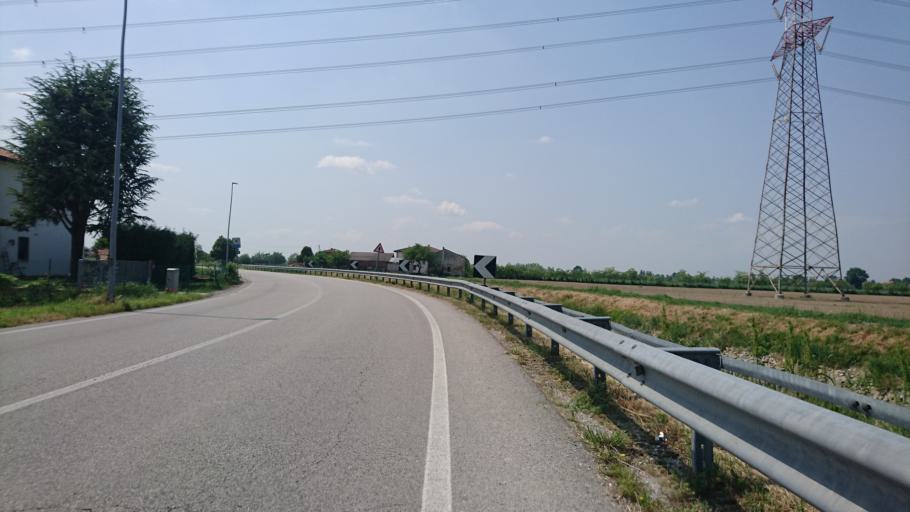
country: IT
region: Veneto
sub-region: Provincia di Venezia
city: Campagna Lupia
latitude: 45.3650
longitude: 12.1256
